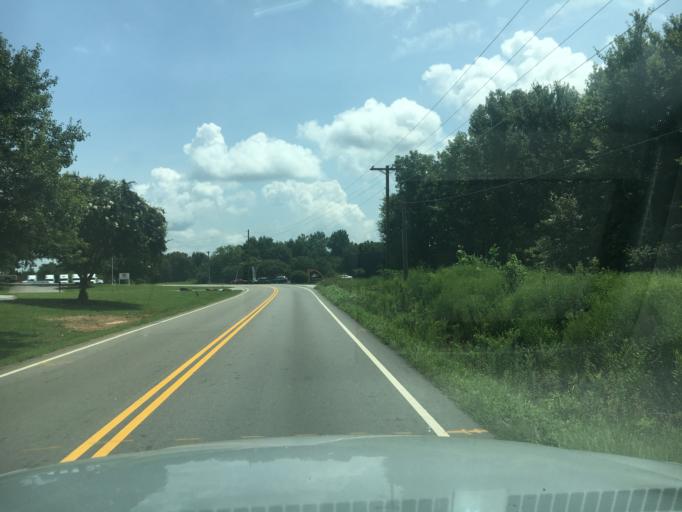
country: US
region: South Carolina
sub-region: Spartanburg County
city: Duncan
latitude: 34.8748
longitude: -82.1432
